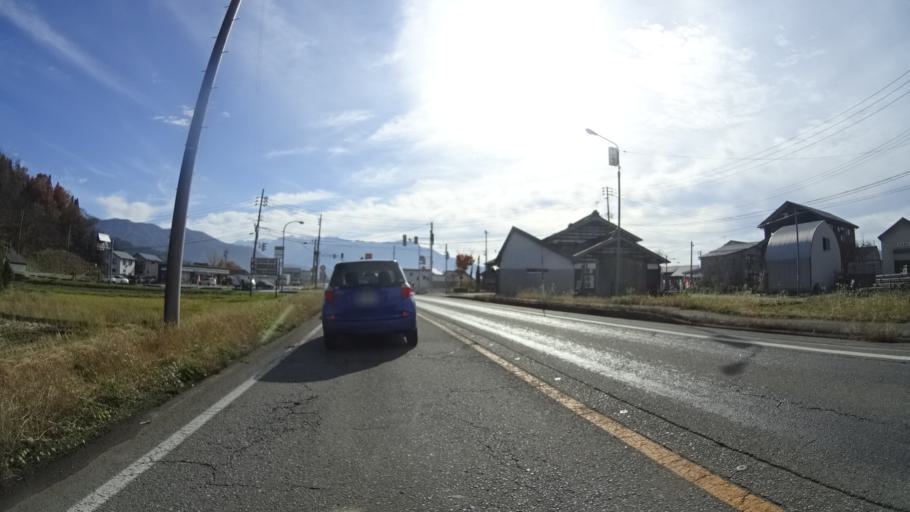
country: JP
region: Niigata
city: Muikamachi
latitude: 37.1158
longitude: 138.9204
